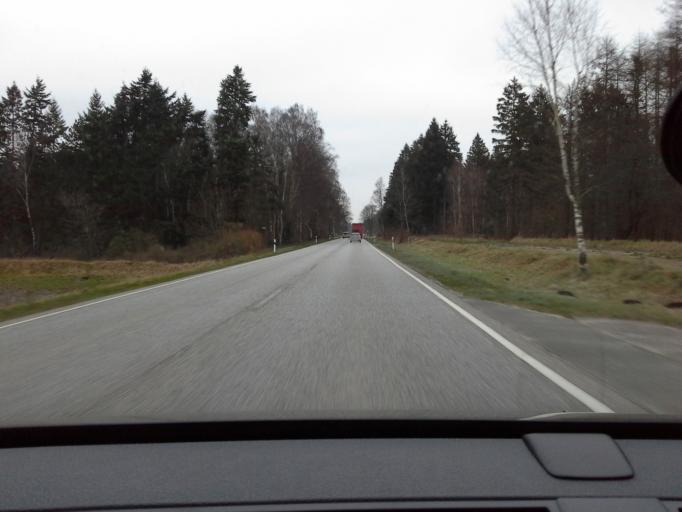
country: DE
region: Schleswig-Holstein
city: Heidmoor
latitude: 53.8303
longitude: 9.8837
